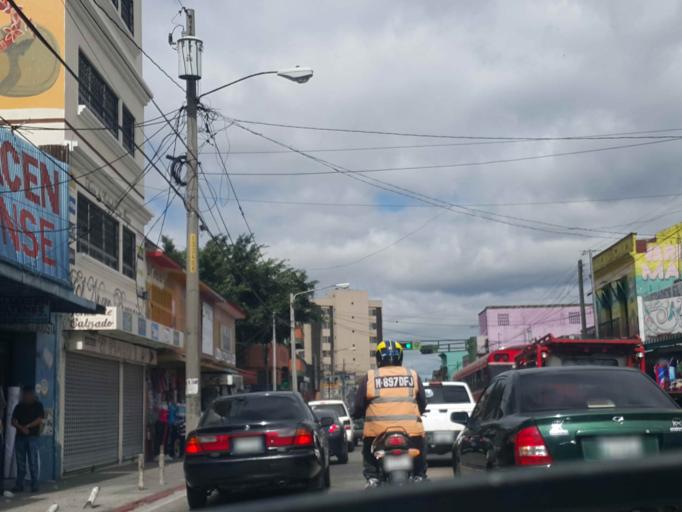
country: GT
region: Guatemala
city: Guatemala City
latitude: 14.6275
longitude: -90.5201
